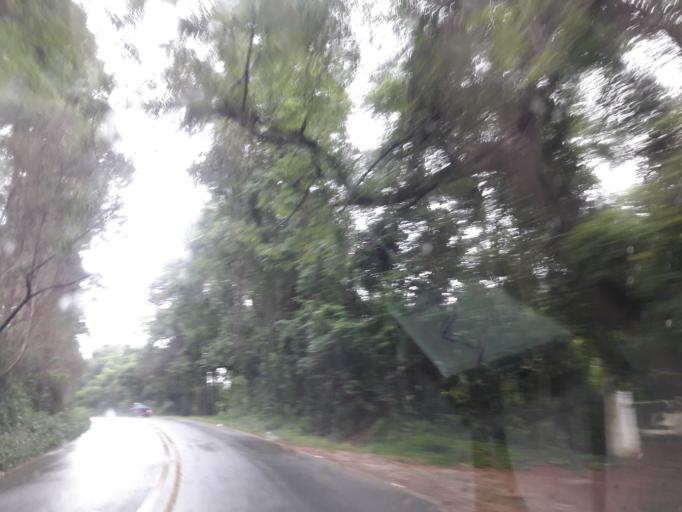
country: BR
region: Sao Paulo
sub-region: Bom Jesus Dos Perdoes
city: Bom Jesus dos Perdoes
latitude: -23.2785
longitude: -46.4221
